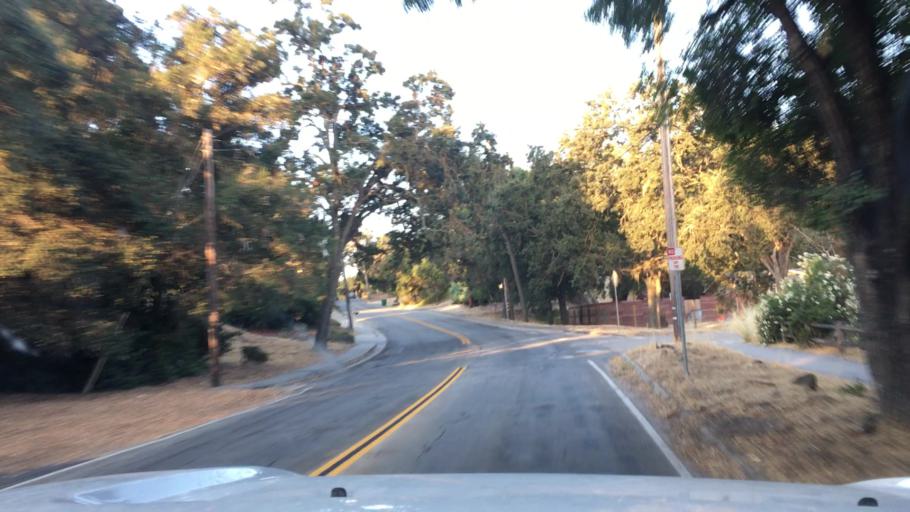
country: US
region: California
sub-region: San Luis Obispo County
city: Atascadero
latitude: 35.4869
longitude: -120.6716
